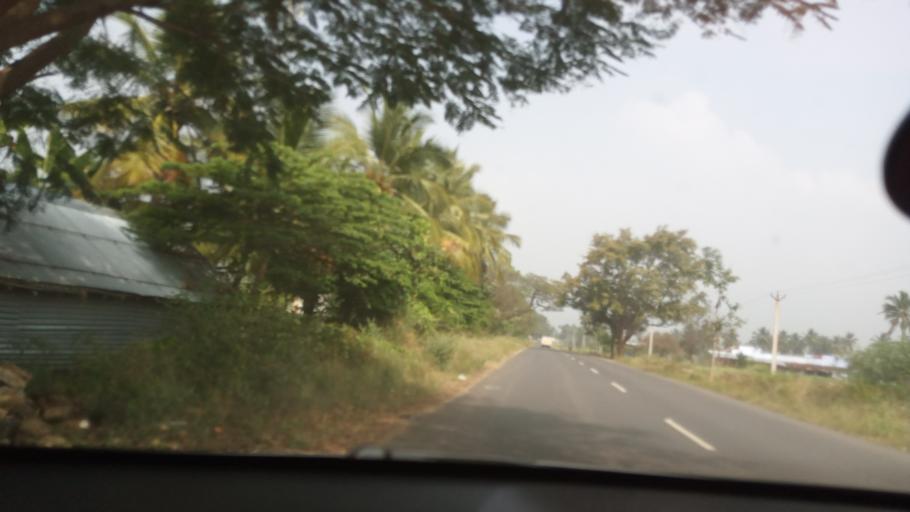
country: IN
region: Tamil Nadu
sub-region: Erode
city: Sathyamangalam
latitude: 11.5345
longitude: 77.1388
